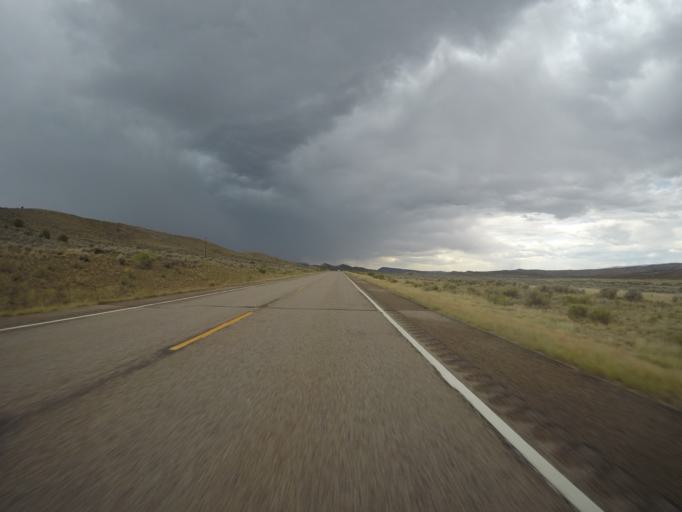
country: US
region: Colorado
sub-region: Rio Blanco County
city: Rangely
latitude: 40.2415
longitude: -108.8939
